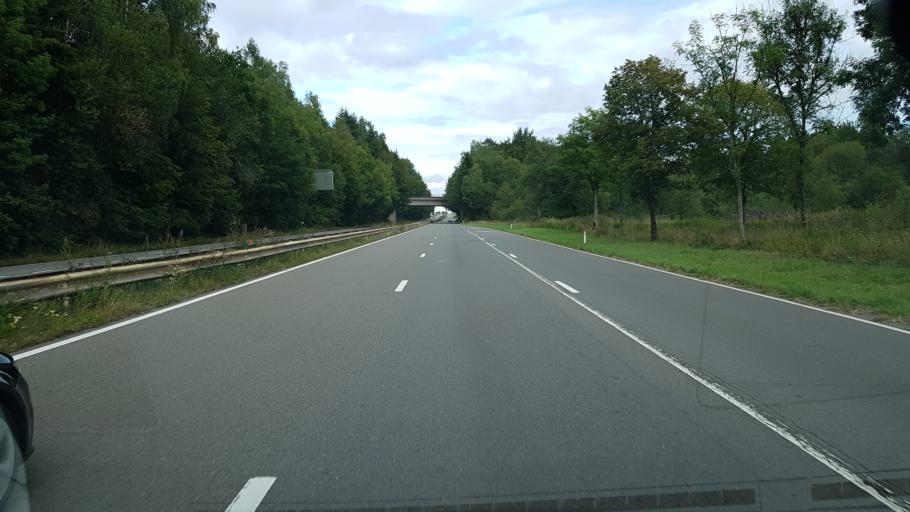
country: BE
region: Wallonia
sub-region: Province du Luxembourg
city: Bertrix
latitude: 49.8689
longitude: 5.2244
